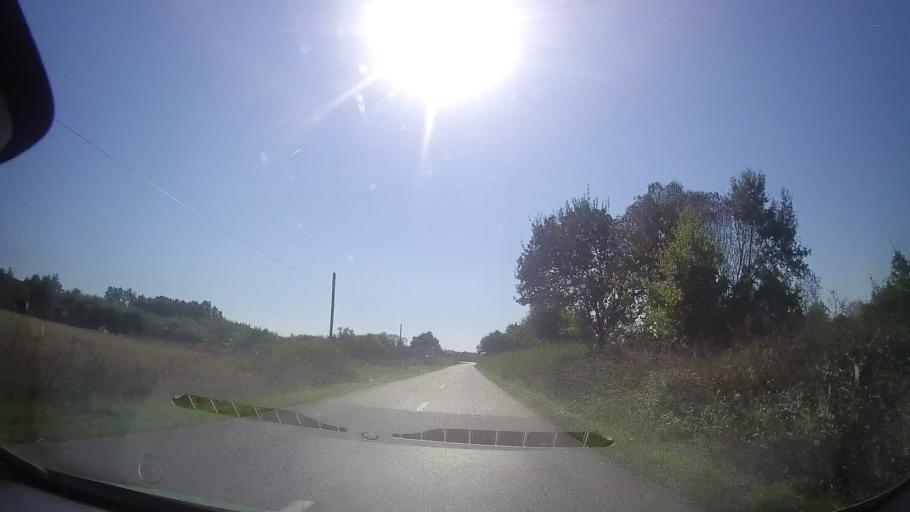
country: RO
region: Timis
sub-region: Comuna Ohaba Lunga
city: Ohaba Lunga
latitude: 45.8722
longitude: 21.9650
